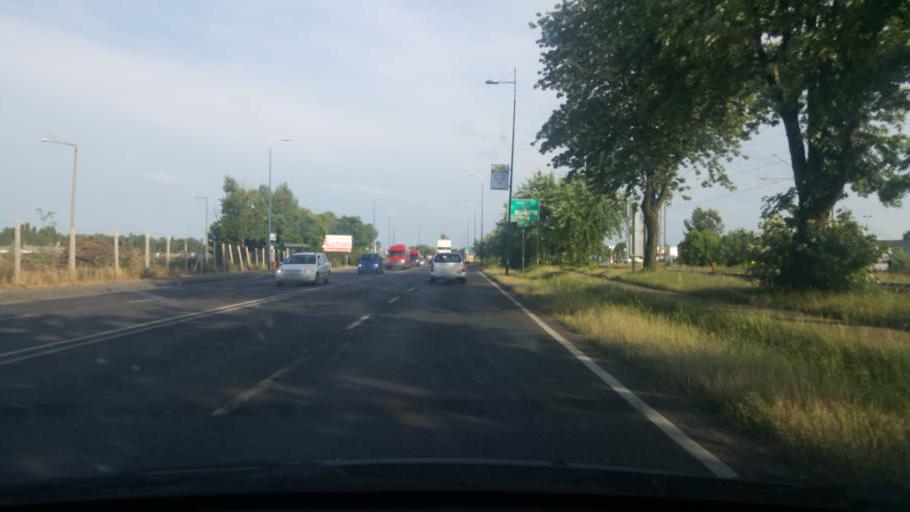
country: HU
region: Pest
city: Gyal
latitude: 47.4233
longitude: 19.2400
